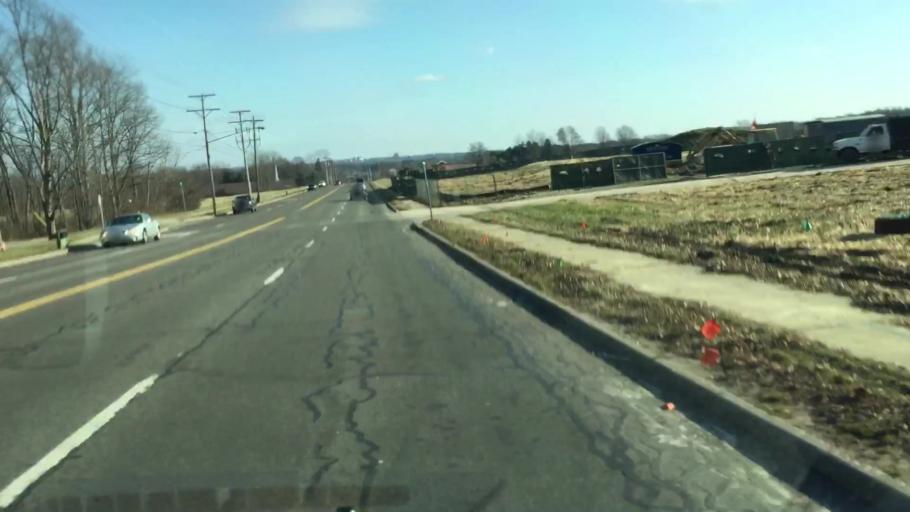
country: US
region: Ohio
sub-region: Summit County
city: Stow
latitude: 41.1581
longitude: -81.4169
